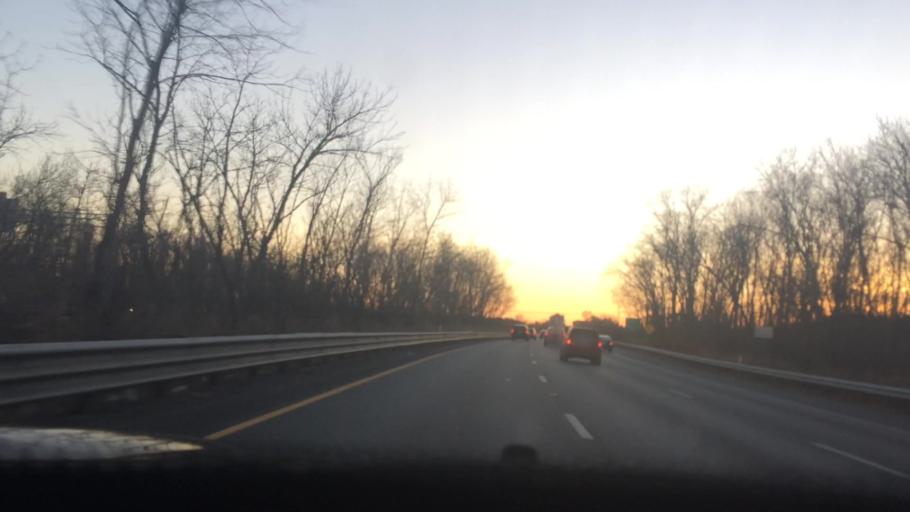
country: US
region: Massachusetts
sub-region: Essex County
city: Haverhill
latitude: 42.7566
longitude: -71.1252
